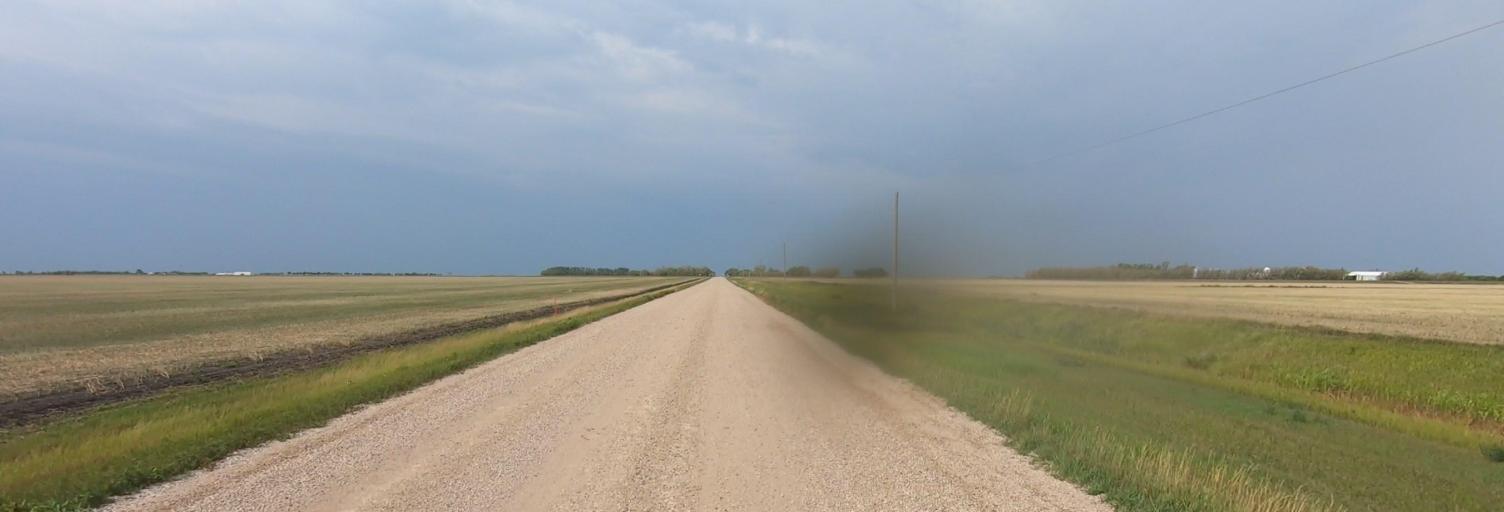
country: CA
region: Manitoba
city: Morris
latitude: 49.5765
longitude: -97.3340
